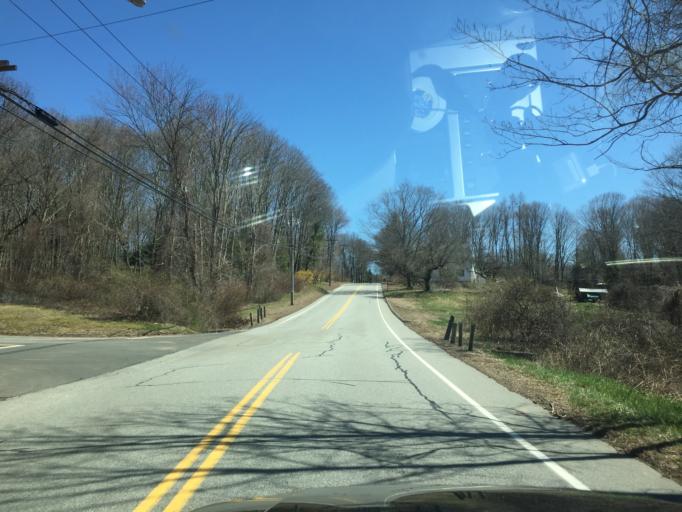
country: US
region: Connecticut
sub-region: Hartford County
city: Terramuggus
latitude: 41.6443
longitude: -72.4773
